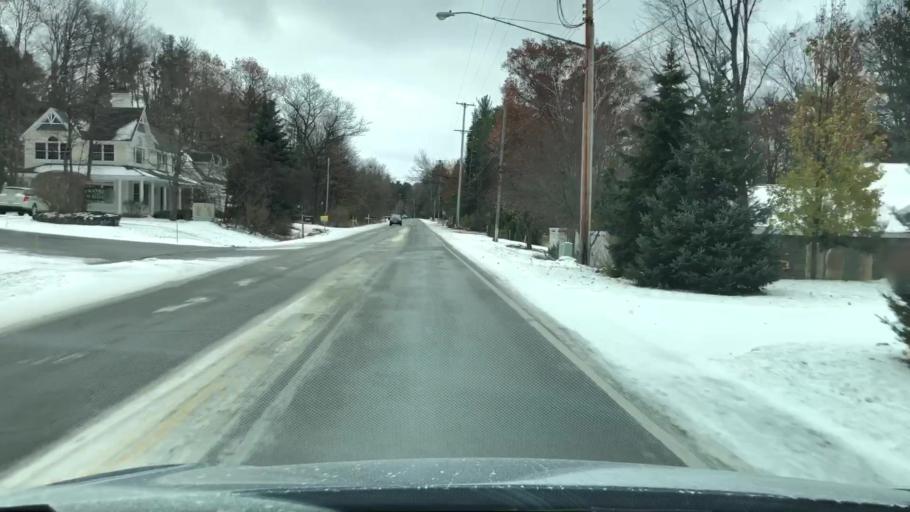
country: US
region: Michigan
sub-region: Grand Traverse County
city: Traverse City
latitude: 44.7811
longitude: -85.5901
